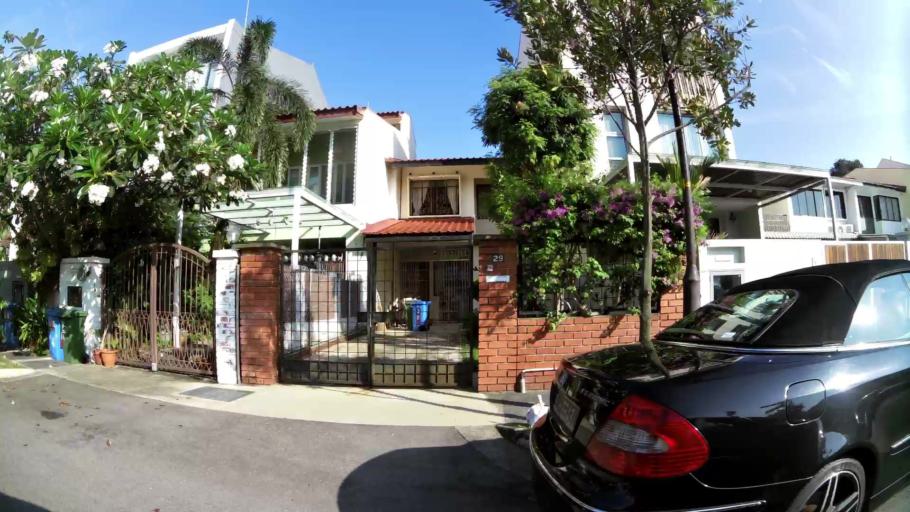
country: SG
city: Singapore
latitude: 1.3150
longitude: 103.9239
